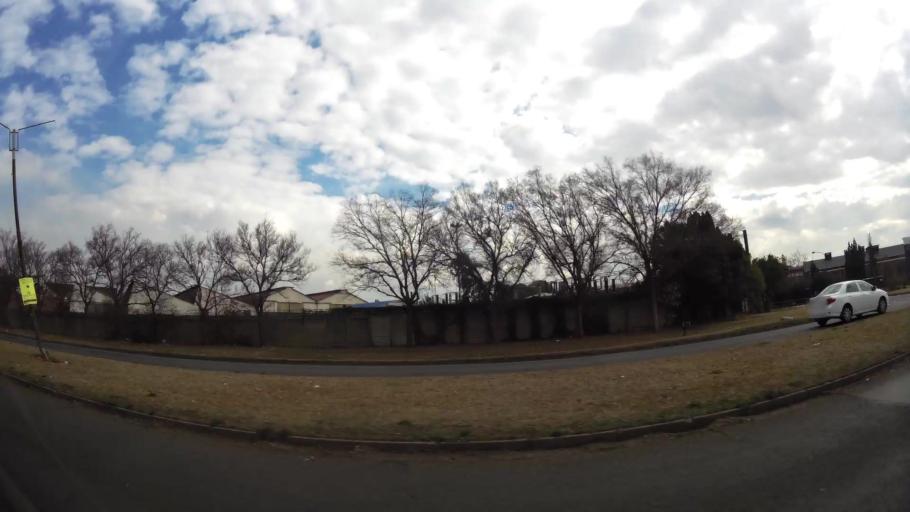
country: ZA
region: Gauteng
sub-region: Sedibeng District Municipality
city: Vereeniging
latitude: -26.6627
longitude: 27.9439
